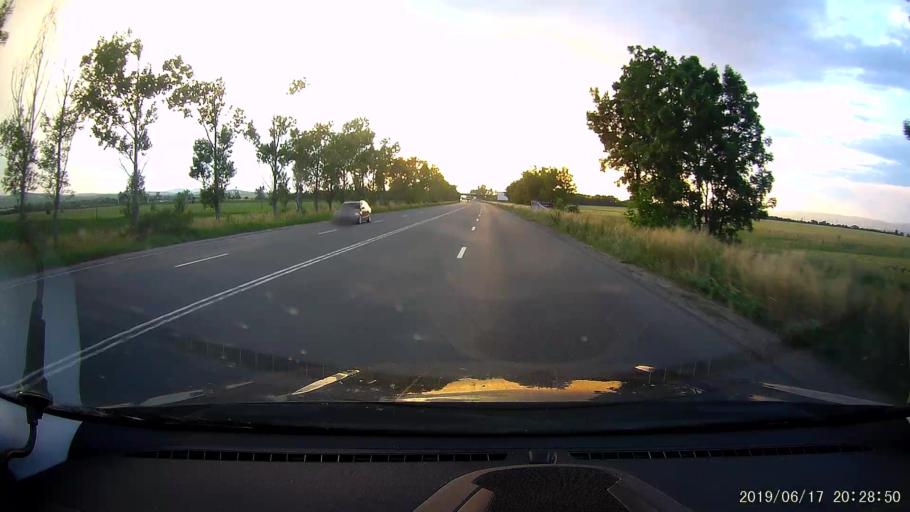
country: BG
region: Sofiya
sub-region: Obshtina Bozhurishte
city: Bozhurishte
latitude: 42.7812
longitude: 23.1715
